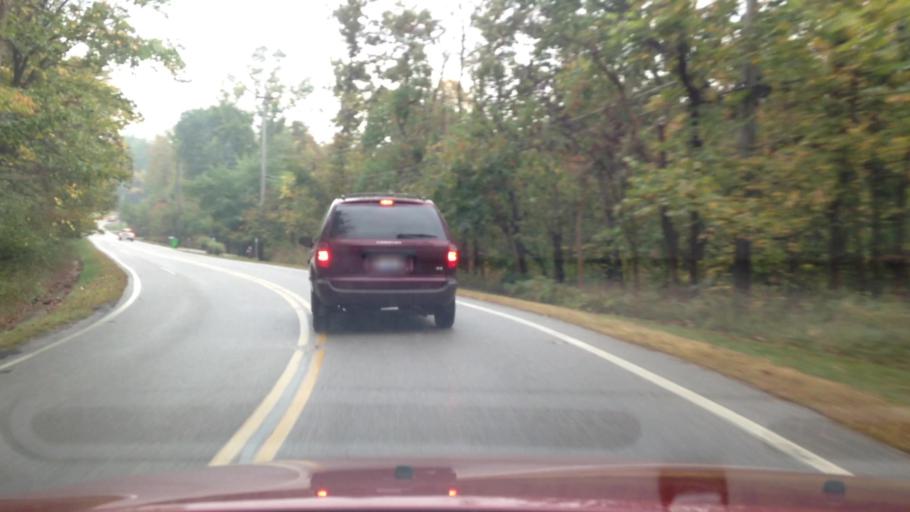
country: US
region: Ohio
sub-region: Cuyahoga County
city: Walton Hills
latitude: 41.3654
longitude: -81.5671
